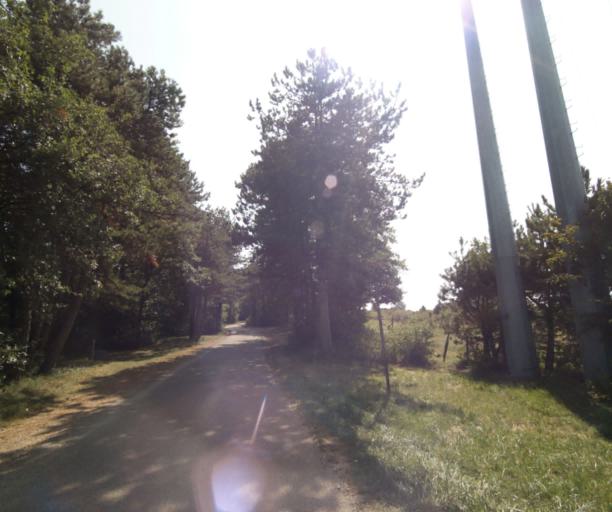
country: FR
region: Bourgogne
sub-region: Departement de Saone-et-Loire
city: Tournus
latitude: 46.5850
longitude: 4.8947
